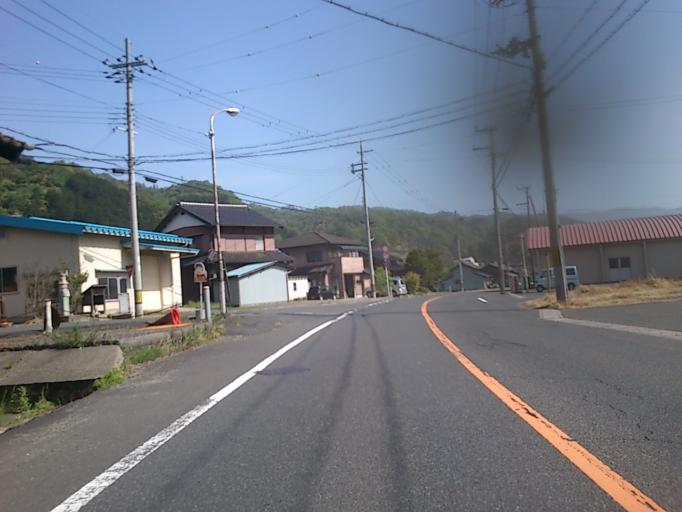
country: JP
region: Kyoto
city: Miyazu
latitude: 35.5564
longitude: 135.1392
